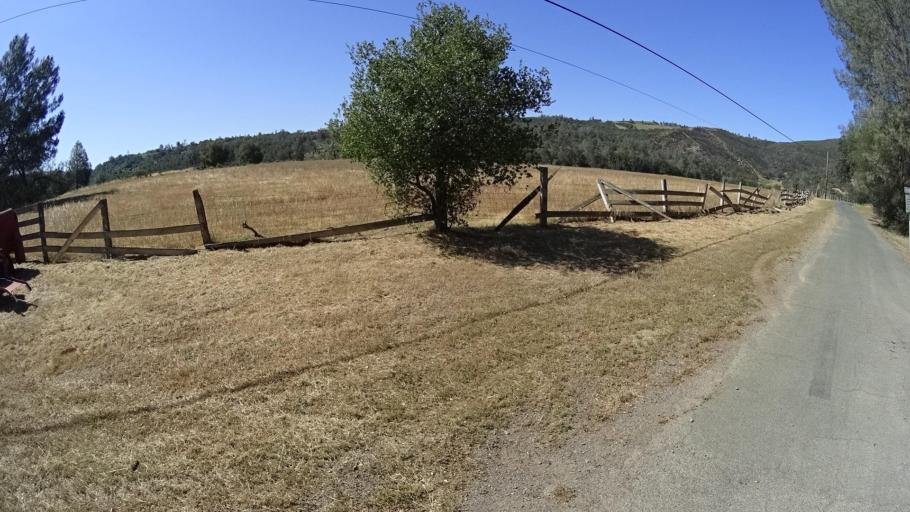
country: US
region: California
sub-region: Lake County
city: Clearlake Oaks
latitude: 39.0568
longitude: -122.5886
